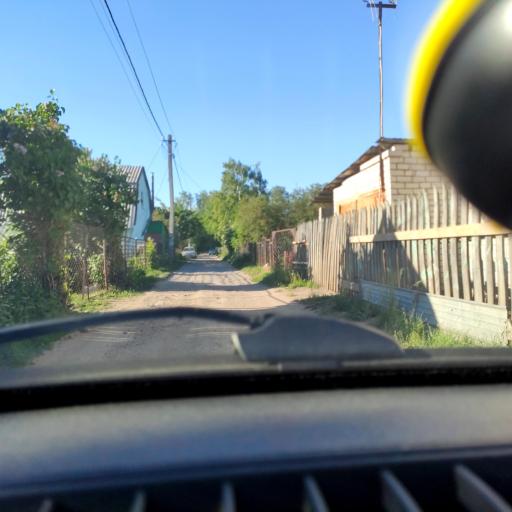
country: RU
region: Samara
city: Tol'yatti
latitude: 53.5967
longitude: 49.3152
